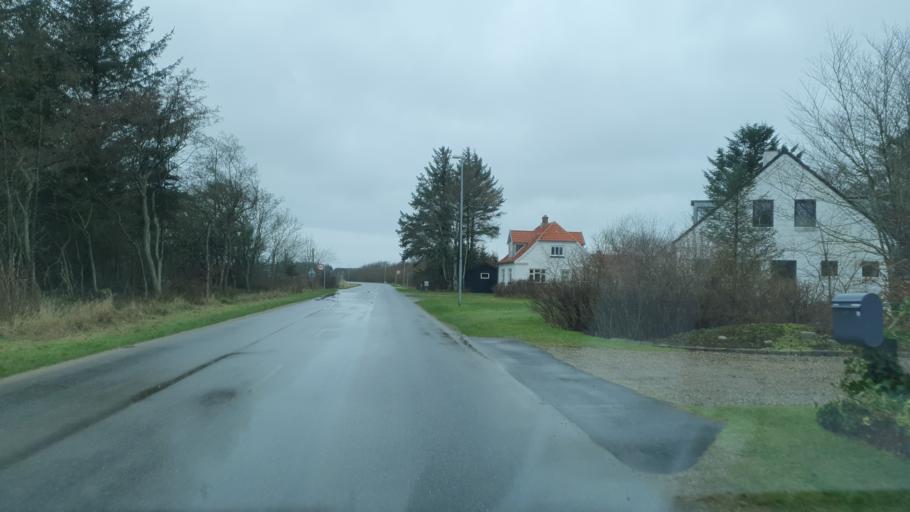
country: DK
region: North Denmark
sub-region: Jammerbugt Kommune
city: Fjerritslev
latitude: 57.1337
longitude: 9.1305
